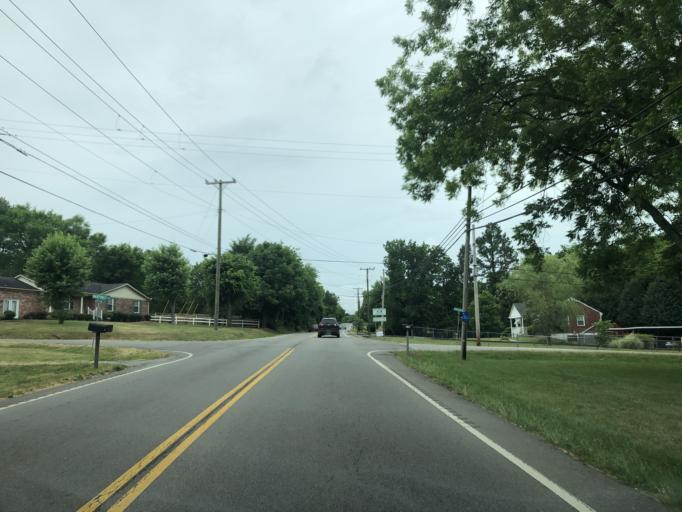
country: US
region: Tennessee
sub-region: Davidson County
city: Goodlettsville
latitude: 36.2715
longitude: -86.7612
